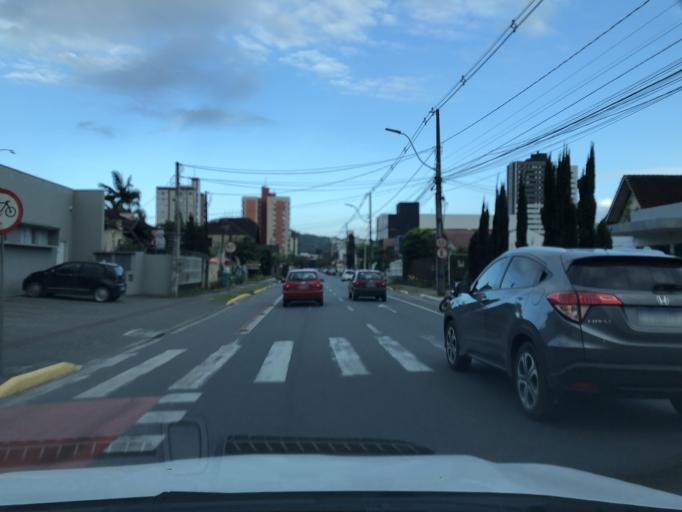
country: BR
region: Santa Catarina
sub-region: Joinville
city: Joinville
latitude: -26.2935
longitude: -48.8526
